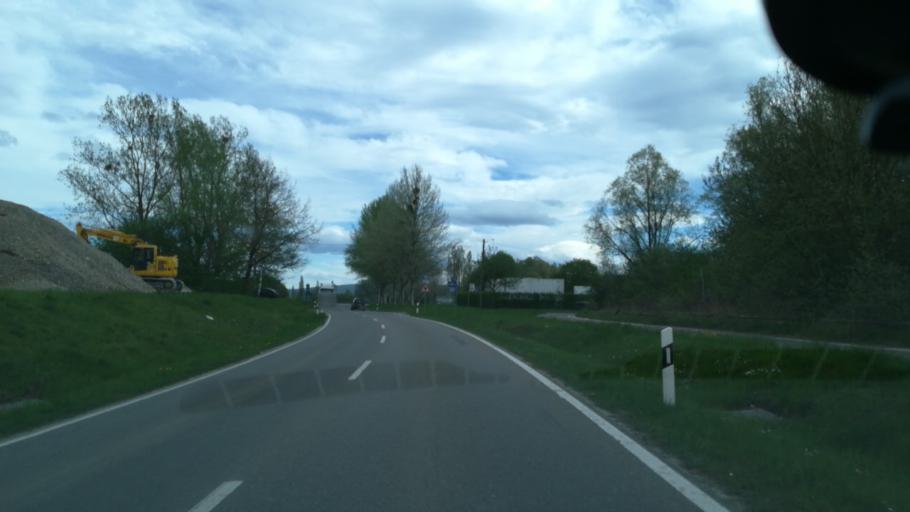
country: DE
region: Baden-Wuerttemberg
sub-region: Freiburg Region
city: Moos
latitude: 47.7484
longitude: 8.9235
